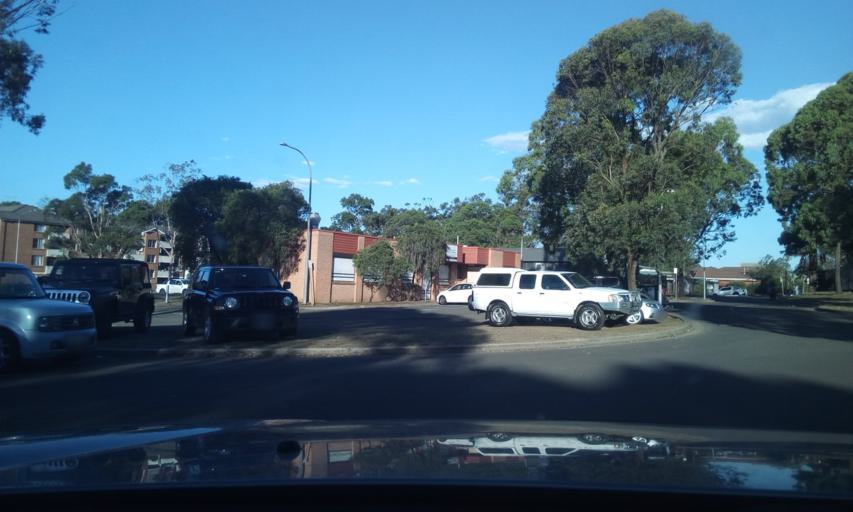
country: AU
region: New South Wales
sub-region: Fairfield
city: Cabramatta West
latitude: -33.9246
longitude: 150.9142
